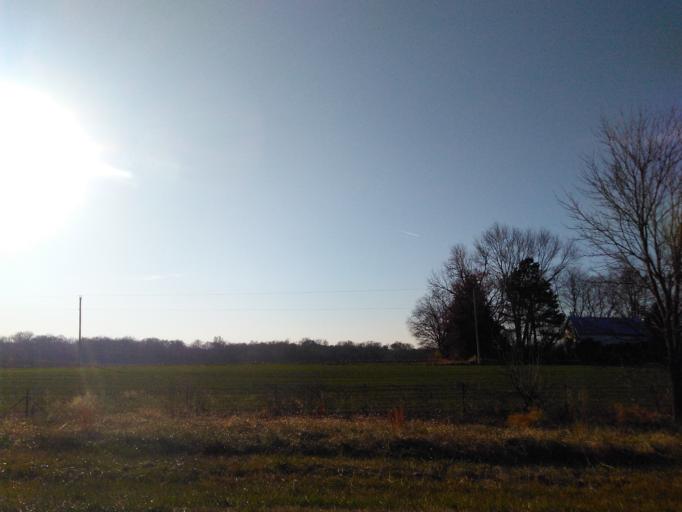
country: US
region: Illinois
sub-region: Madison County
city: Saint Jacob
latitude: 38.7659
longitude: -89.7625
